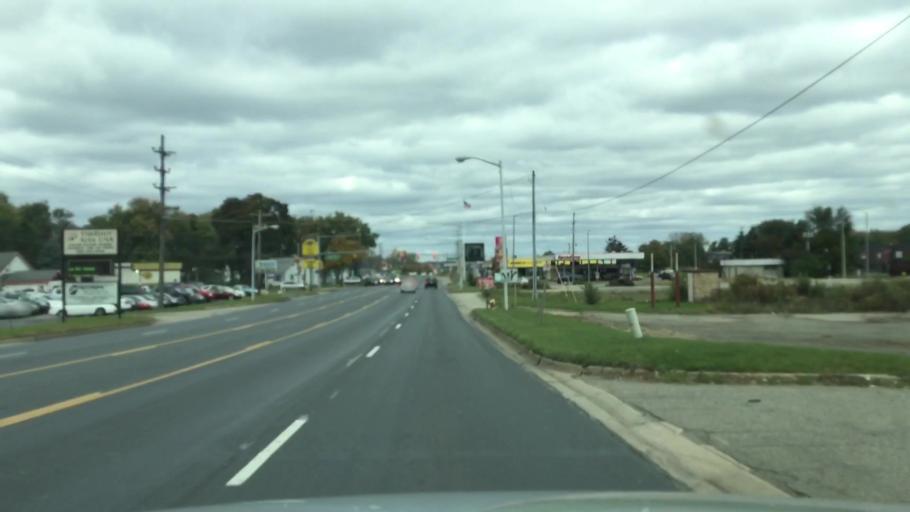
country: US
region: Michigan
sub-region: Kalamazoo County
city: Eastwood
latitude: 42.2651
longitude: -85.5307
